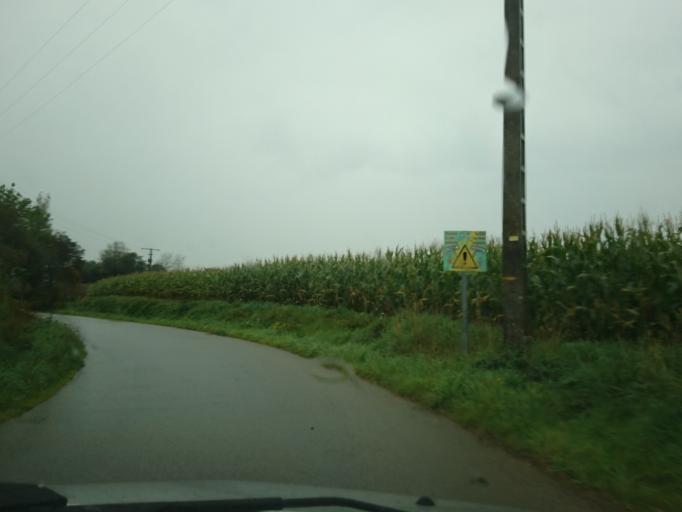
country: FR
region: Brittany
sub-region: Departement du Finistere
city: Kernilis
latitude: 48.5540
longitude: -4.3959
